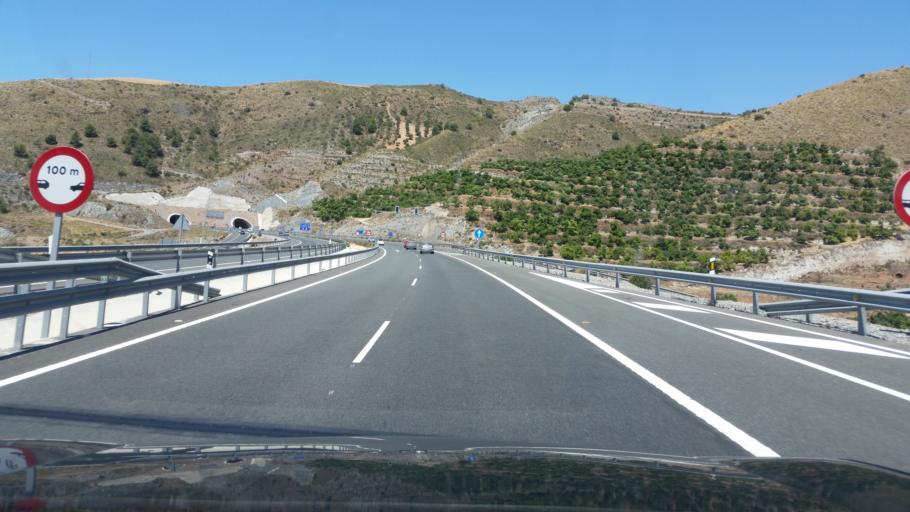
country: ES
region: Andalusia
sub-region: Provincia de Granada
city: Gualchos
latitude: 36.7201
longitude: -3.4322
